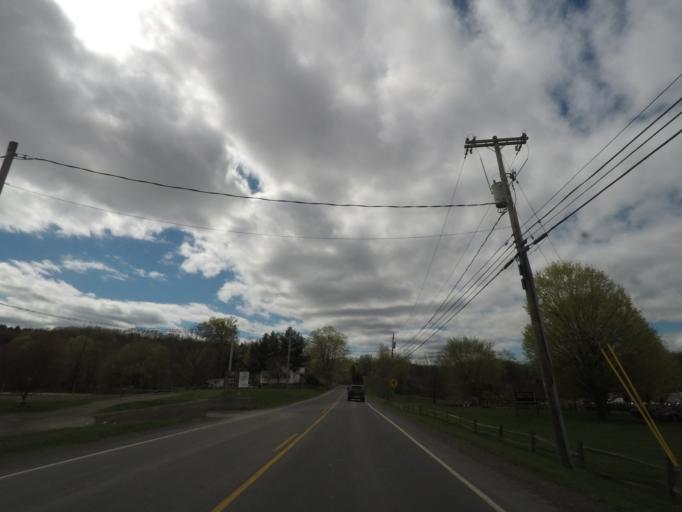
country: US
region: New York
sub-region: Columbia County
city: Chatham
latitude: 42.3764
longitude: -73.6341
